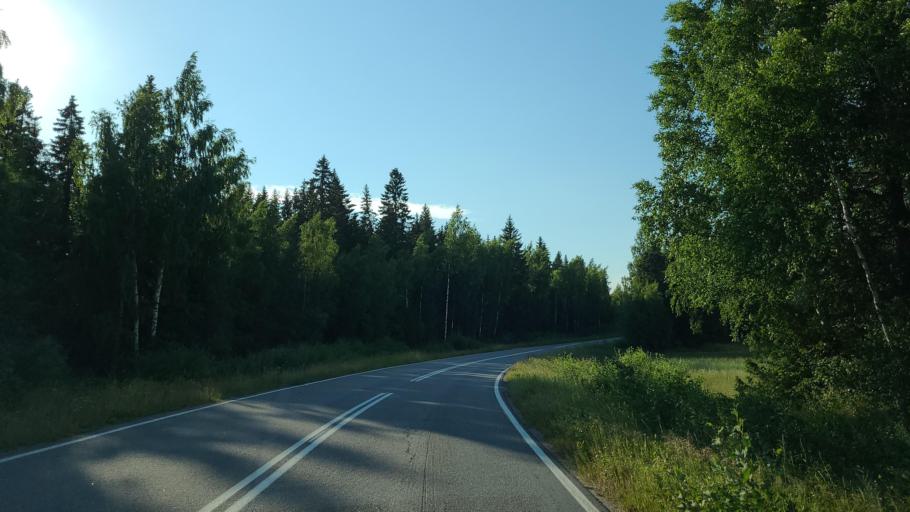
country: FI
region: Ostrobothnia
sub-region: Vaasa
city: Replot
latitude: 63.3221
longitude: 21.3462
